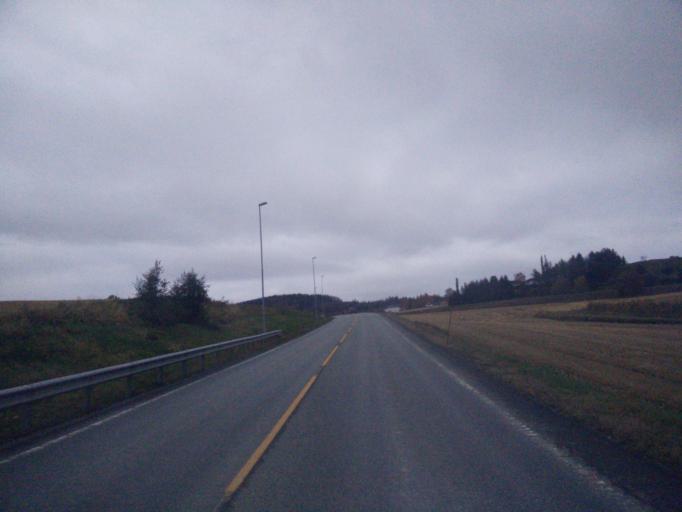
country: NO
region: Nord-Trondelag
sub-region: Stjordal
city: Stjordal
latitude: 63.5001
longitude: 10.8646
